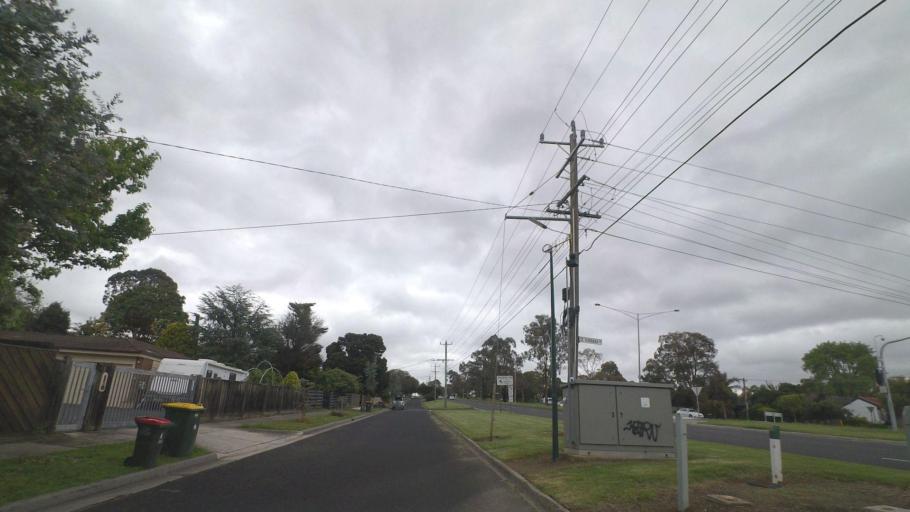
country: AU
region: Victoria
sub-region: Whitehorse
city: Vermont South
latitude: -37.8579
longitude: 145.1902
